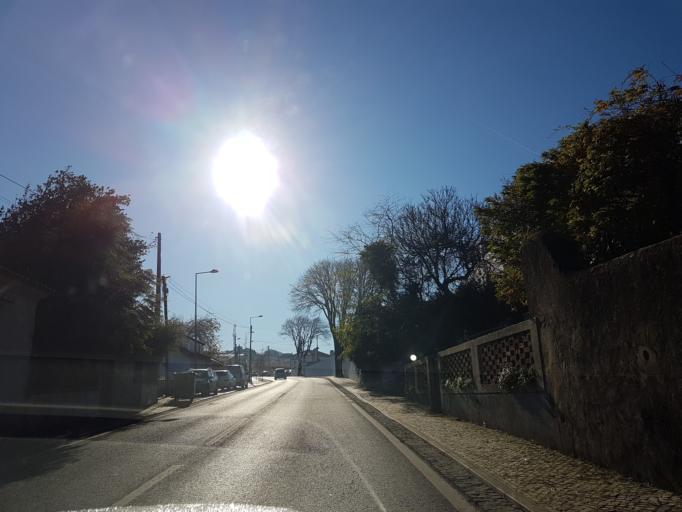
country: PT
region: Lisbon
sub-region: Sintra
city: Sintra
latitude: 38.7938
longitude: -9.3741
